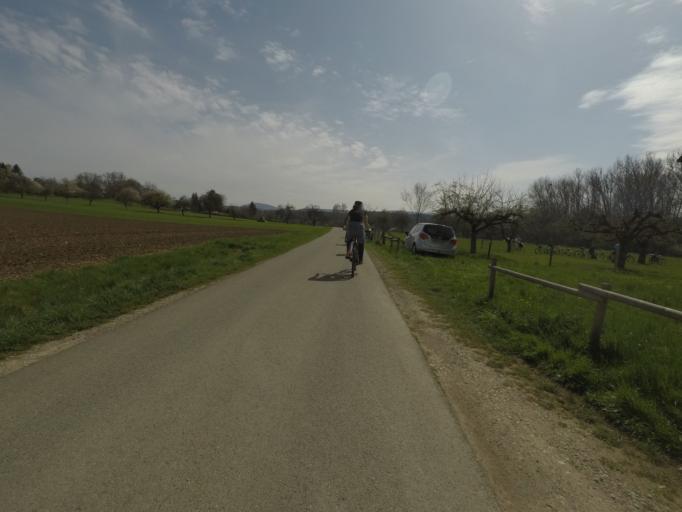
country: DE
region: Baden-Wuerttemberg
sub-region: Tuebingen Region
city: Reutlingen
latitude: 48.4894
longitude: 9.1710
